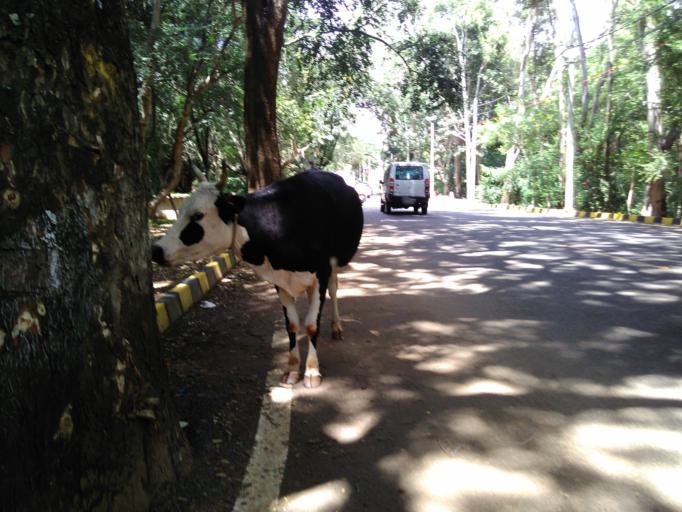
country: IN
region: Karnataka
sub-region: Mysore
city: Mysore
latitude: 12.3139
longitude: 76.6270
